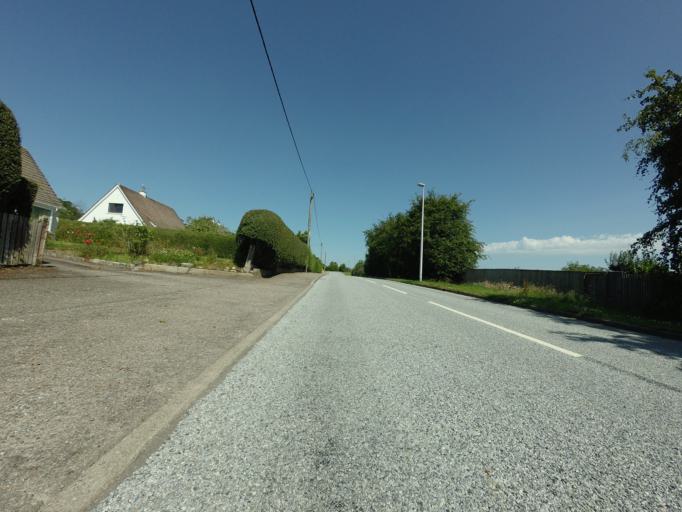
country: GB
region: Scotland
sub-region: Highland
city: Dingwall
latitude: 57.6063
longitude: -4.4249
